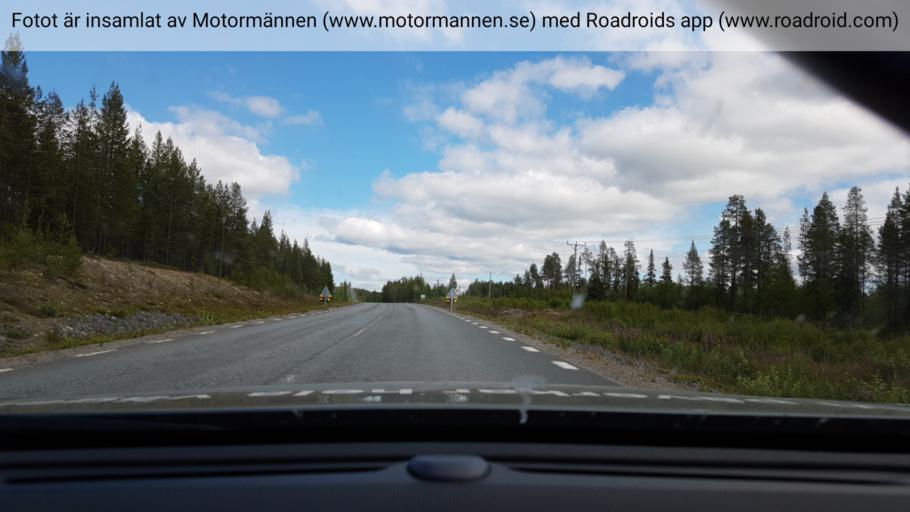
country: SE
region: Vaesterbotten
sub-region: Sorsele Kommun
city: Sorsele
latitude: 65.5373
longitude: 17.5824
